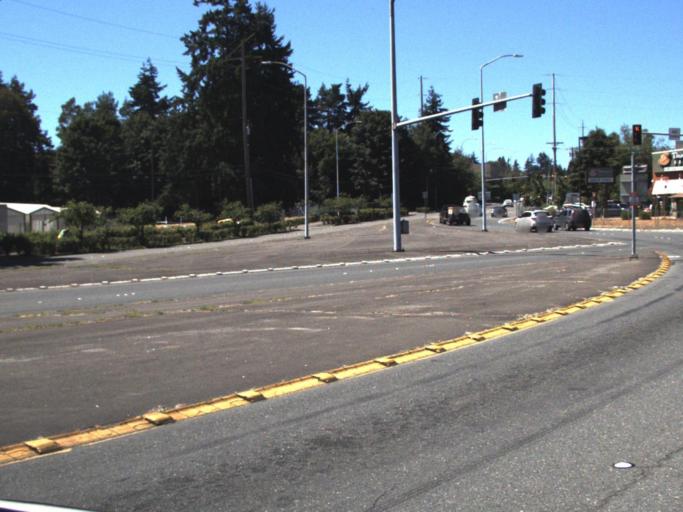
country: US
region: Washington
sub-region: Jefferson County
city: Port Hadlock-Irondale
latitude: 47.9521
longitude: -122.8835
